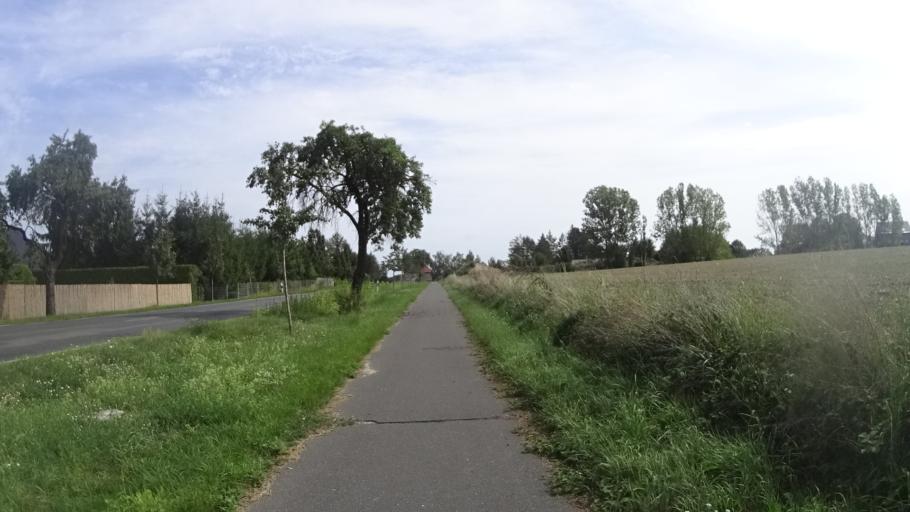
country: DE
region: Brandenburg
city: Gross Kreutz
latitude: 52.3109
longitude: 12.7302
